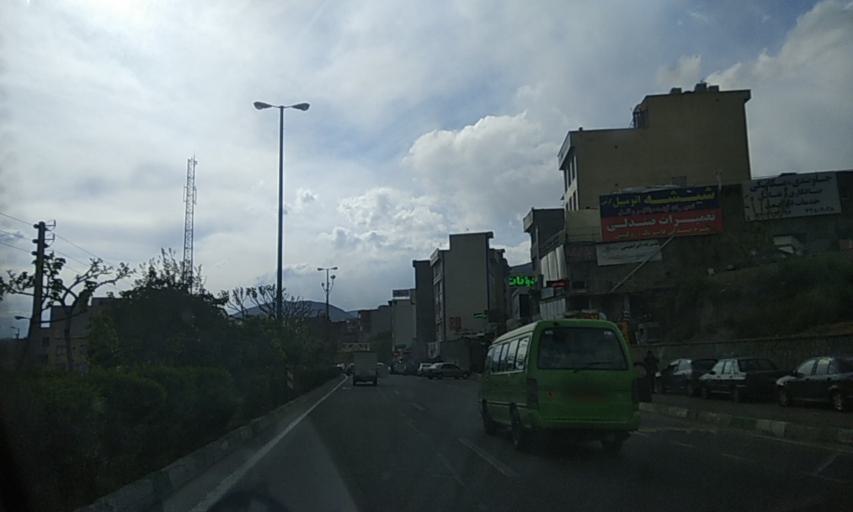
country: IR
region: Tehran
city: Tajrish
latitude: 35.7788
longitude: 51.3120
